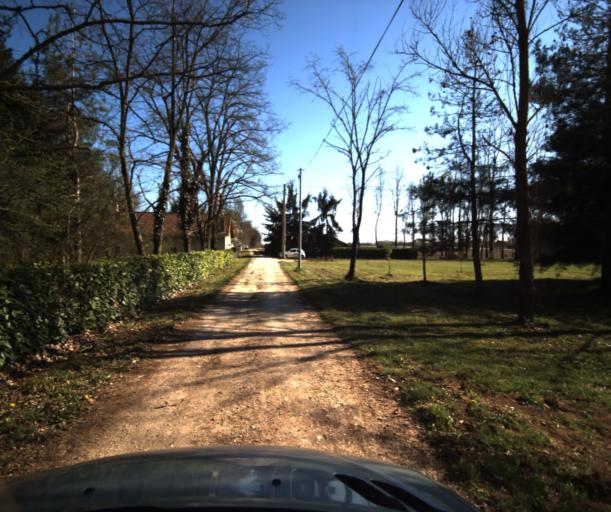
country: FR
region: Midi-Pyrenees
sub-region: Departement du Tarn-et-Garonne
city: Bressols
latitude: 43.9626
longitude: 1.3456
